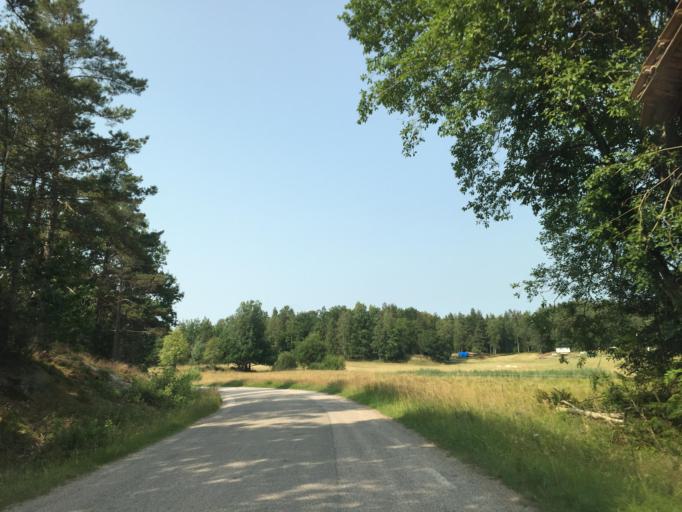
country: SE
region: Vaestra Goetaland
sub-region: Trollhattan
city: Sjuntorp
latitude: 58.2982
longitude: 12.1447
